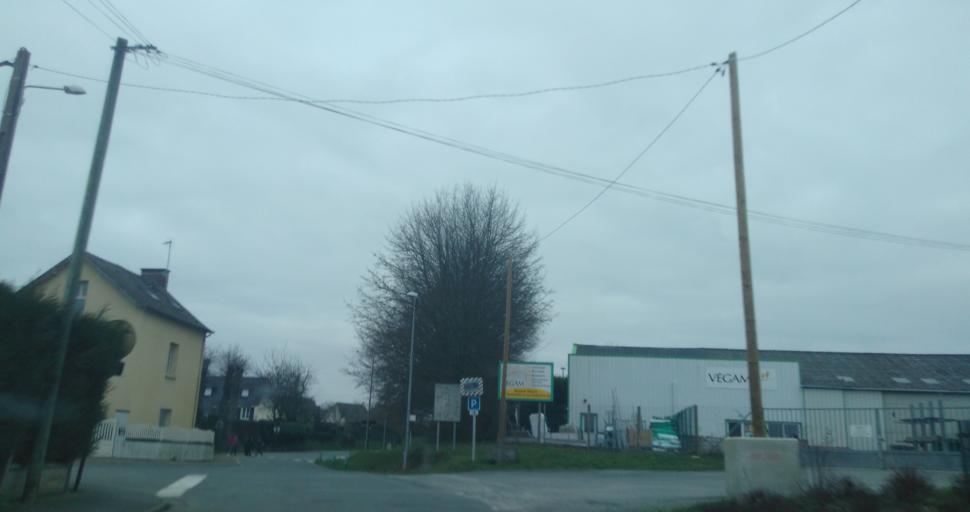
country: FR
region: Brittany
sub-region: Departement d'Ille-et-Vilaine
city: Romille
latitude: 48.2191
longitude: -1.8917
